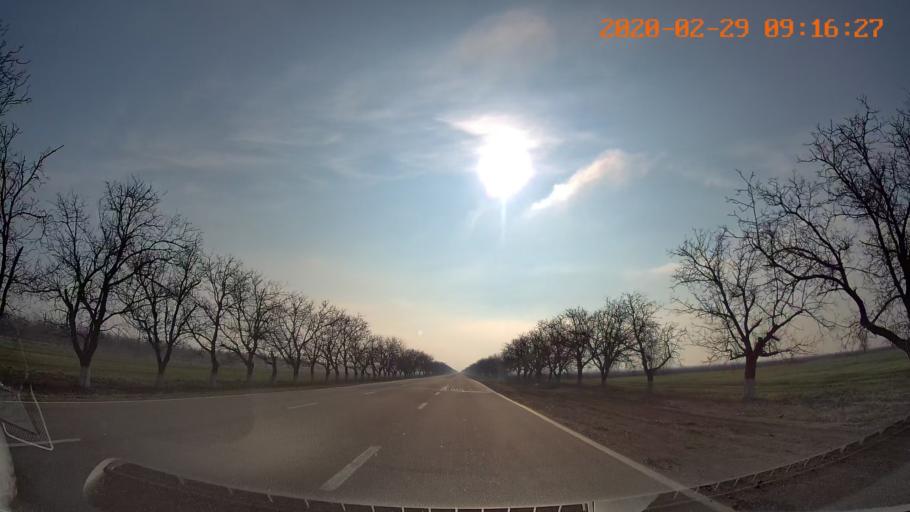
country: MD
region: Telenesti
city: Pervomaisc
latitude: 46.7918
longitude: 29.8866
